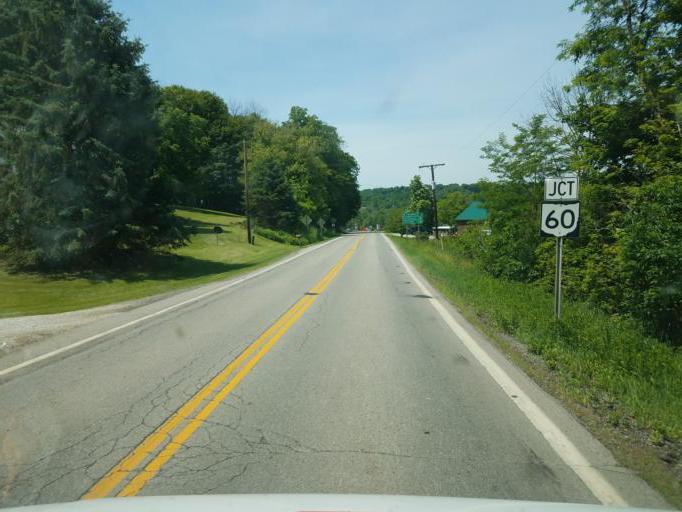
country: US
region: Ohio
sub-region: Ashland County
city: Loudonville
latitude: 40.7073
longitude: -82.2409
